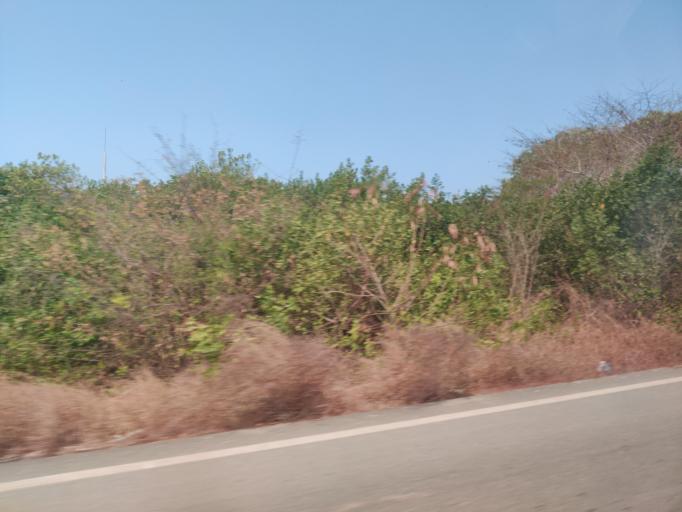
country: CO
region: Bolivar
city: Turbana
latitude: 10.1790
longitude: -75.6452
